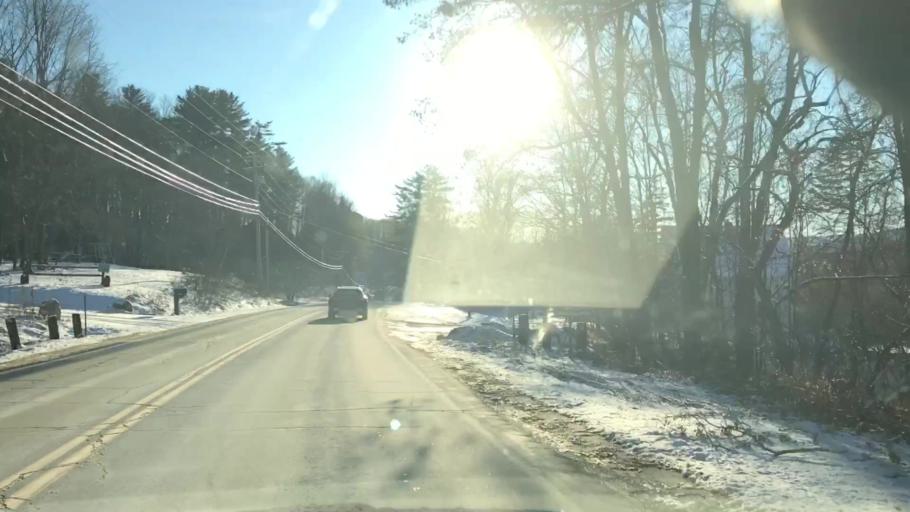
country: US
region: New Hampshire
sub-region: Grafton County
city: Haverhill
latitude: 44.0458
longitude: -72.0553
